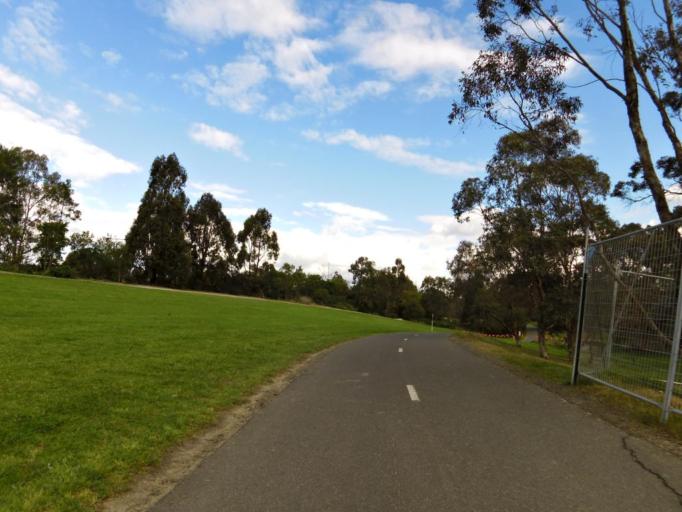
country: AU
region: Victoria
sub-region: Boroondara
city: Balwyn North
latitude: -37.7845
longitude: 145.0990
